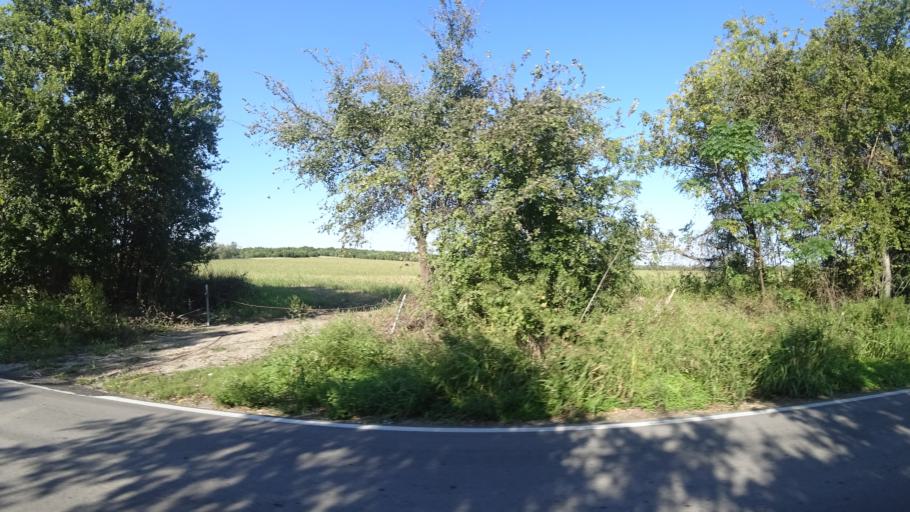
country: US
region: Texas
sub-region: Travis County
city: Manor
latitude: 30.3403
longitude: -97.6599
